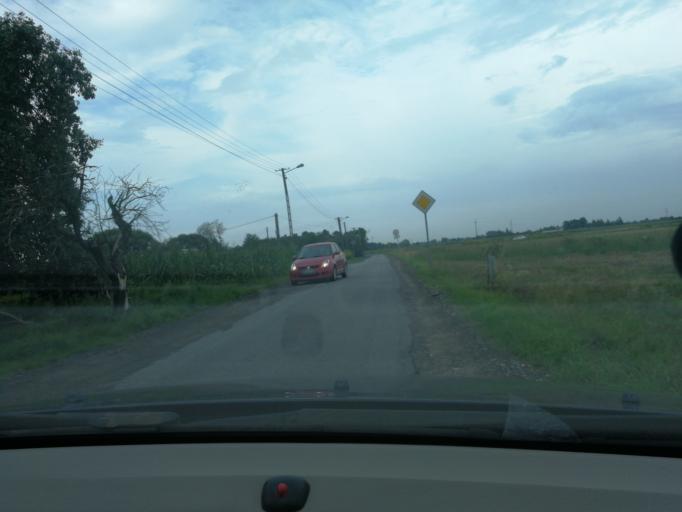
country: PL
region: Masovian Voivodeship
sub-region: Powiat grodziski
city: Grodzisk Mazowiecki
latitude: 52.1210
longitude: 20.5782
